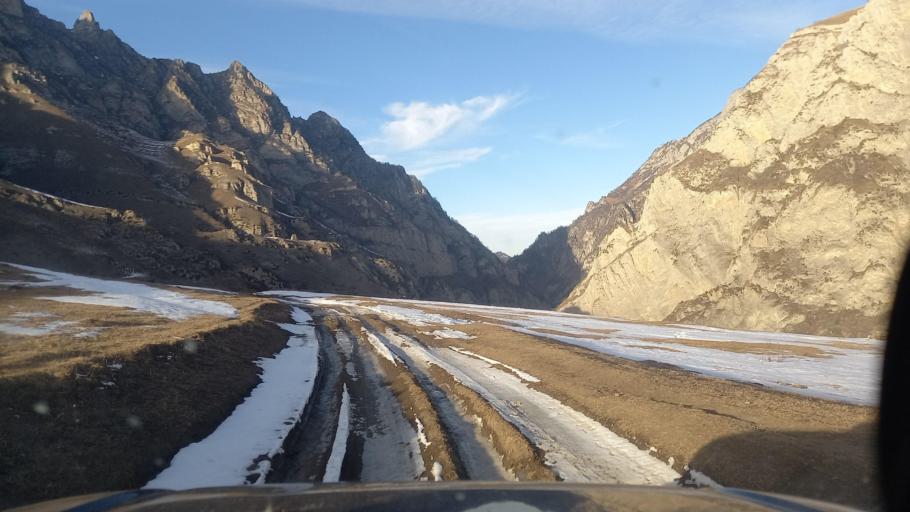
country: RU
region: Ingushetiya
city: Dzhayrakh
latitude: 42.8550
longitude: 44.5158
